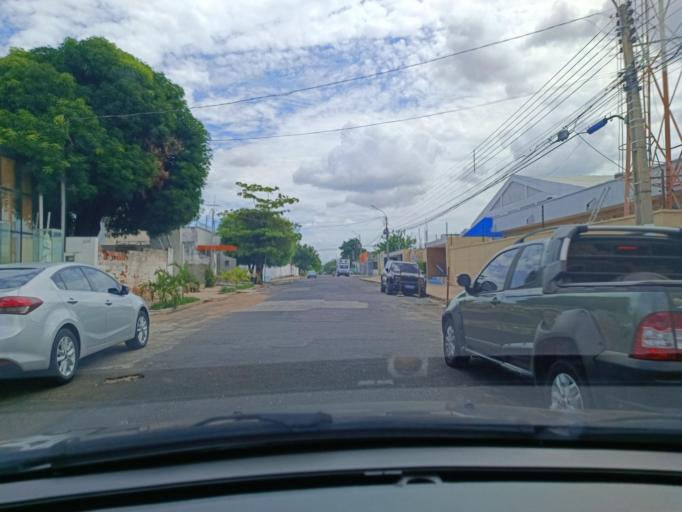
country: BR
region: Piaui
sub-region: Teresina
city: Teresina
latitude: -5.0872
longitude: -42.8003
